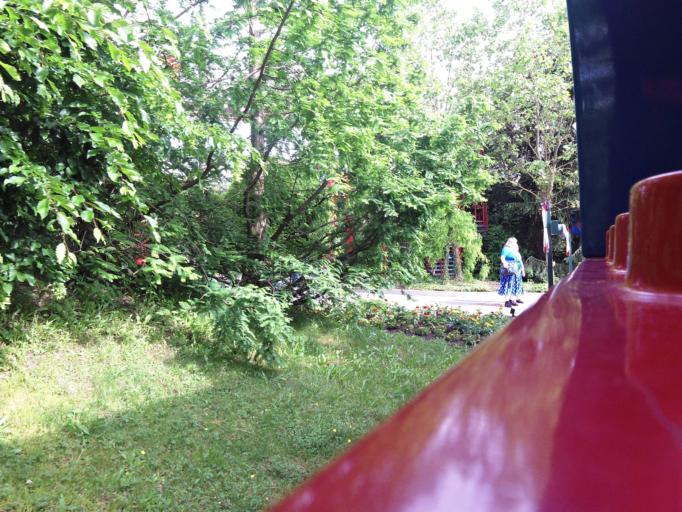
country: DE
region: Bavaria
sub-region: Swabia
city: Wasserburg
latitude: 48.4243
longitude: 10.3019
